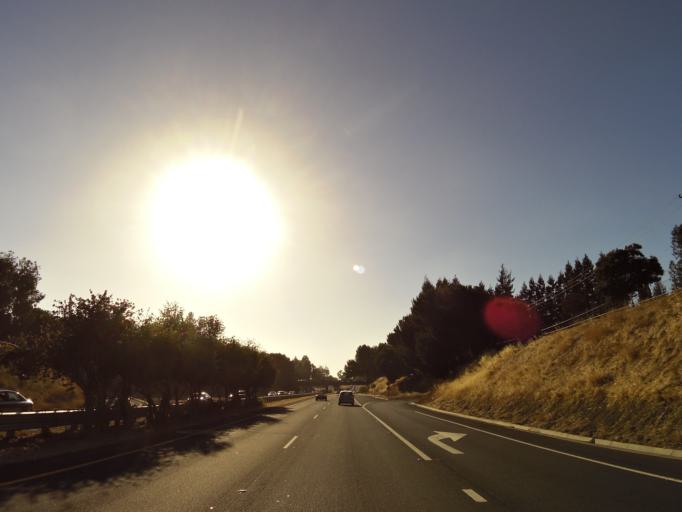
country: US
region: California
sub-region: Santa Clara County
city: Sunnyvale
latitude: 37.3836
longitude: -122.0287
